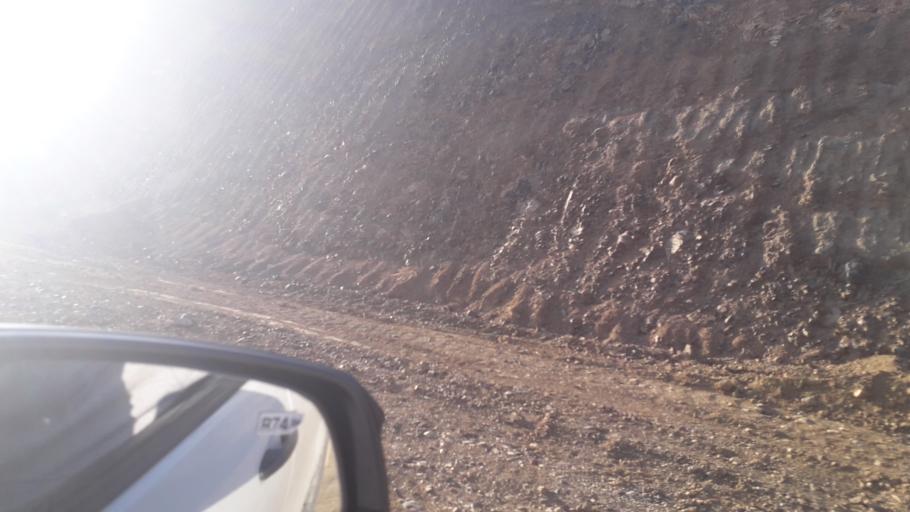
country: ET
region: Amhara
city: Dese
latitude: 11.5185
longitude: 39.2484
